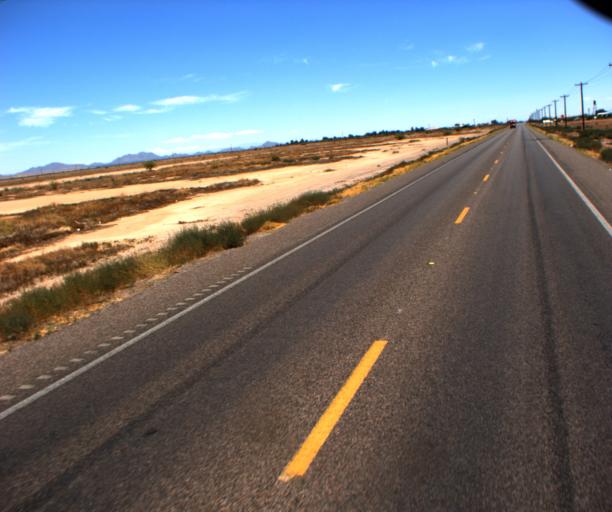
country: US
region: Arizona
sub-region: Pinal County
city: Casa Grande
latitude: 32.8794
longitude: -111.8854
